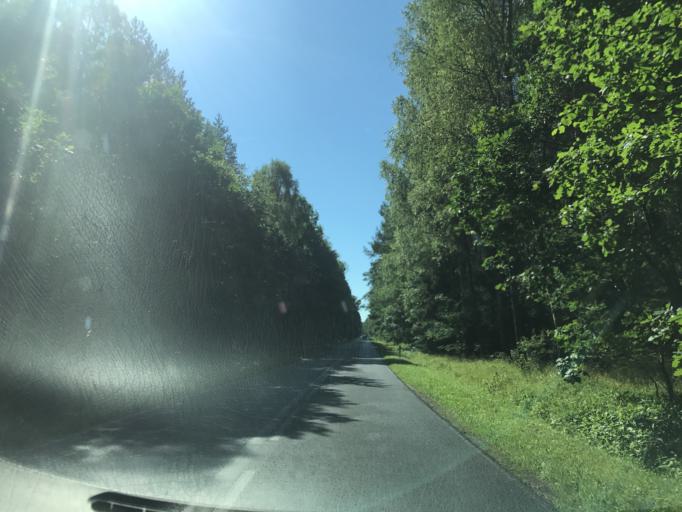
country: PL
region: Pomeranian Voivodeship
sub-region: Powiat slupski
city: Potegowo
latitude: 54.3970
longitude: 17.4678
